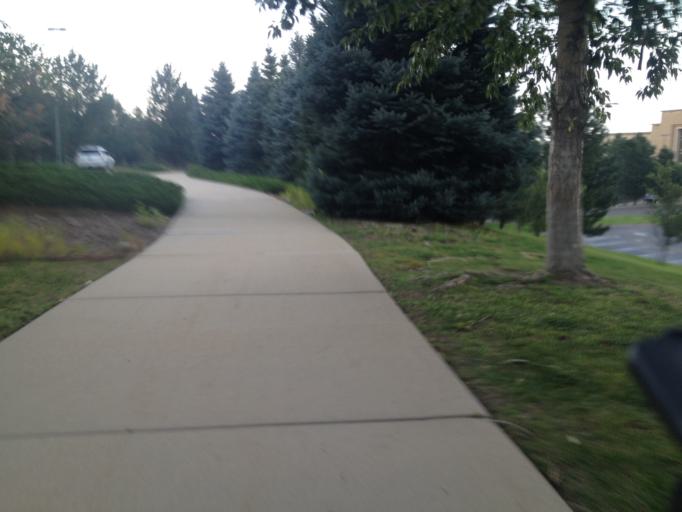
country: US
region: Colorado
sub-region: Boulder County
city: Superior
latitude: 39.9326
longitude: -105.1372
